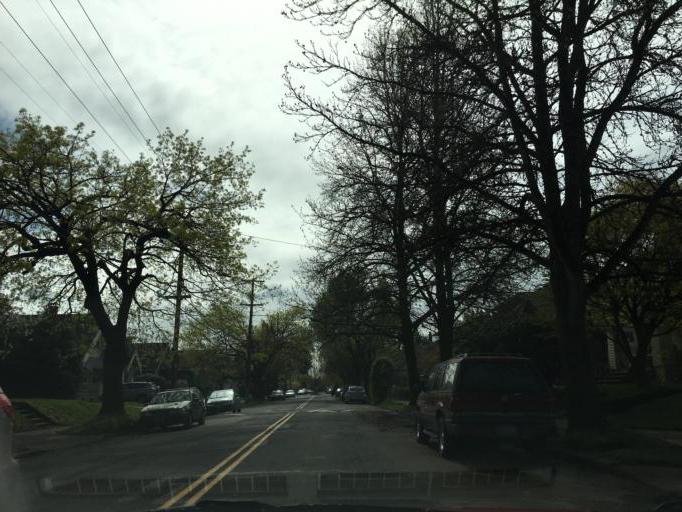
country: US
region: Oregon
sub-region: Clackamas County
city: Milwaukie
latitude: 45.4733
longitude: -122.6477
